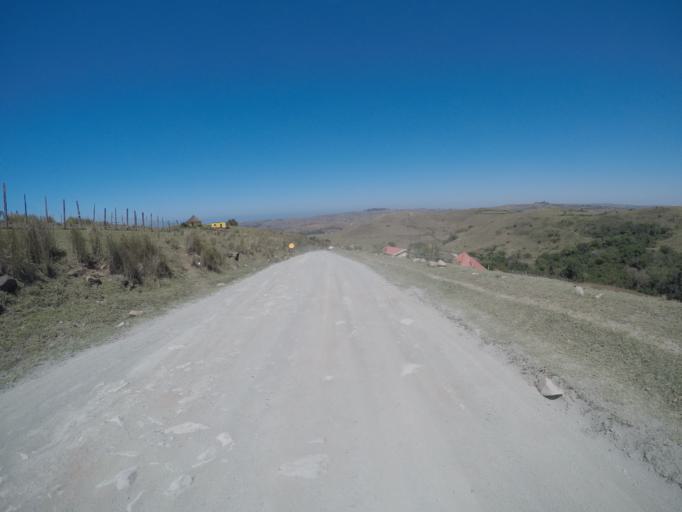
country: ZA
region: Eastern Cape
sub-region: OR Tambo District Municipality
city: Libode
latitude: -32.0100
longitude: 29.0733
